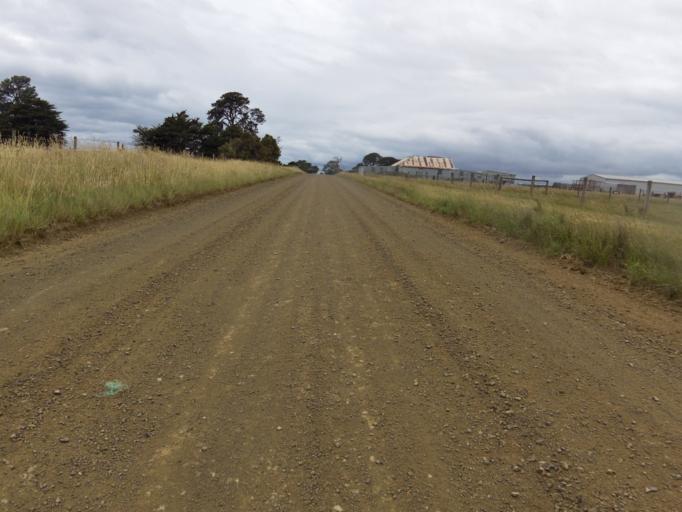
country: AU
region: Victoria
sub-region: Bass Coast
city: Cowes
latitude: -38.3891
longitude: 145.3453
